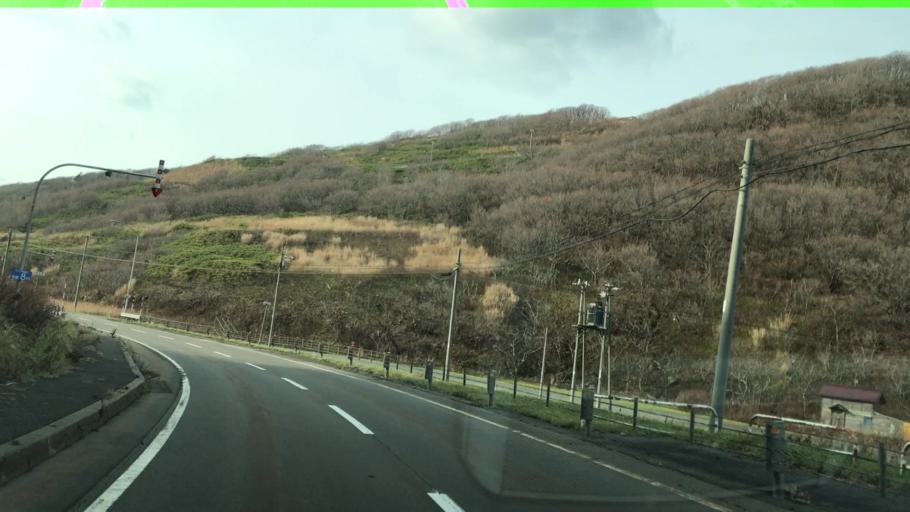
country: JP
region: Hokkaido
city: Iwanai
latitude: 43.3294
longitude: 140.3666
